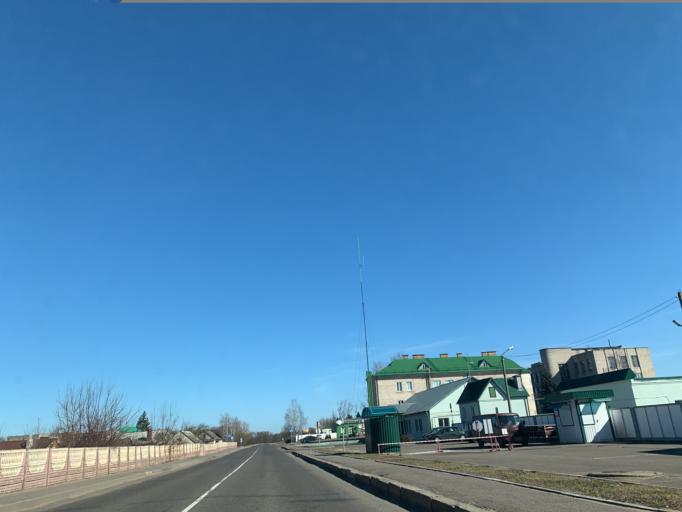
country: BY
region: Minsk
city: Nyasvizh
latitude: 53.2143
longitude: 26.6989
